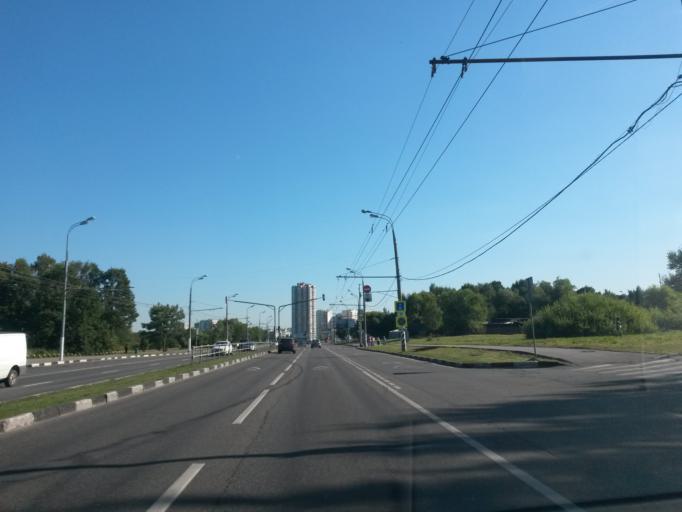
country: RU
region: Moscow
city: Yasenevo
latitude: 55.6256
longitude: 37.5416
